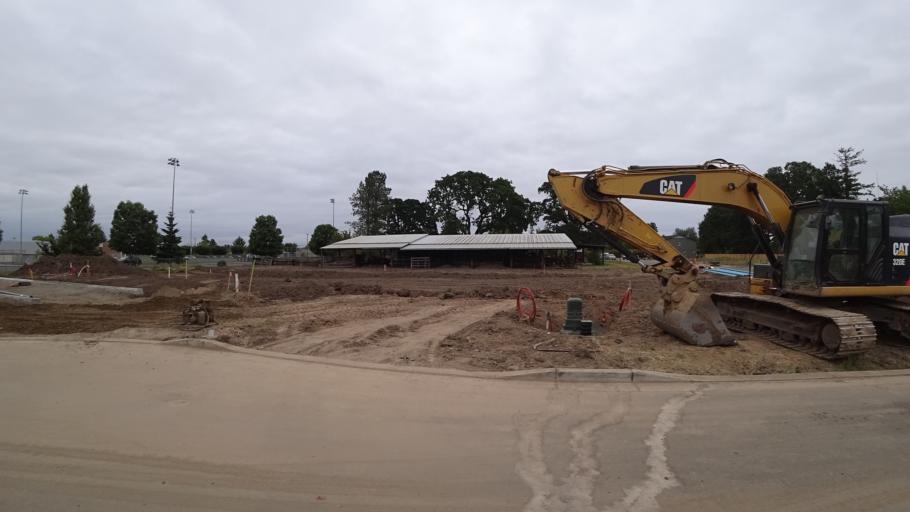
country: US
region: Oregon
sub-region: Washington County
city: Hillsboro
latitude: 45.4916
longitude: -122.9325
